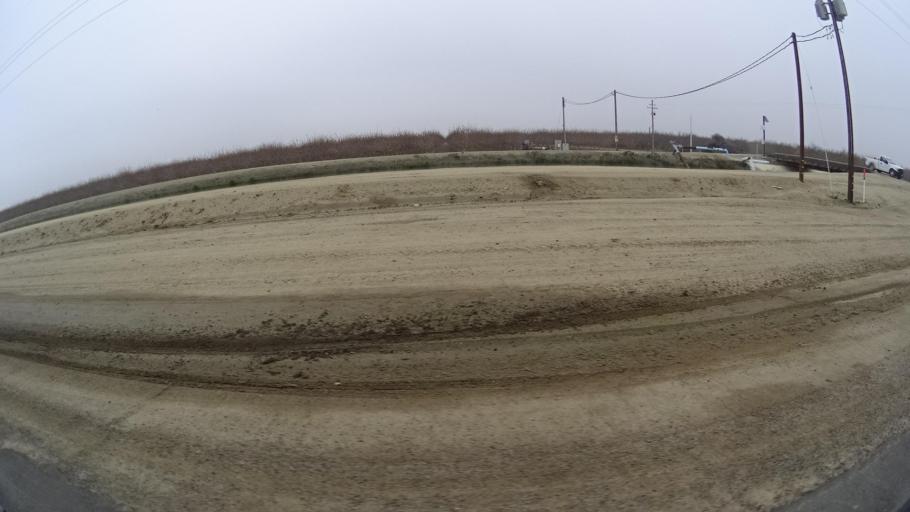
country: US
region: California
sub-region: Kern County
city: Wasco
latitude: 35.6962
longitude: -119.4017
